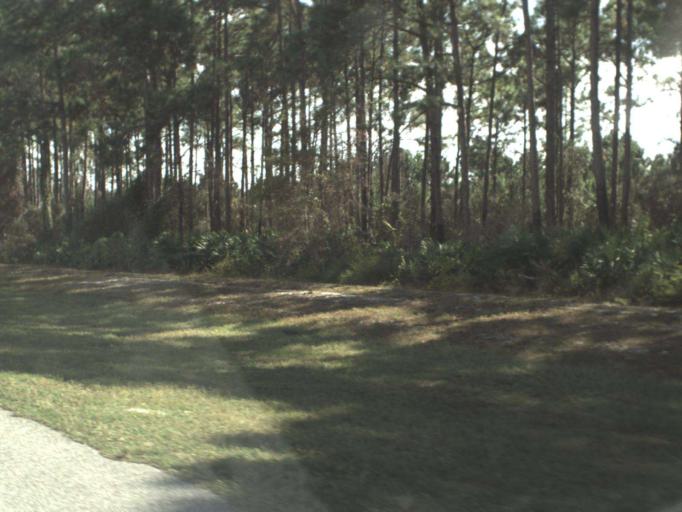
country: US
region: Florida
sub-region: Bay County
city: Tyndall Air Force Base
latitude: 30.0573
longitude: -85.5739
